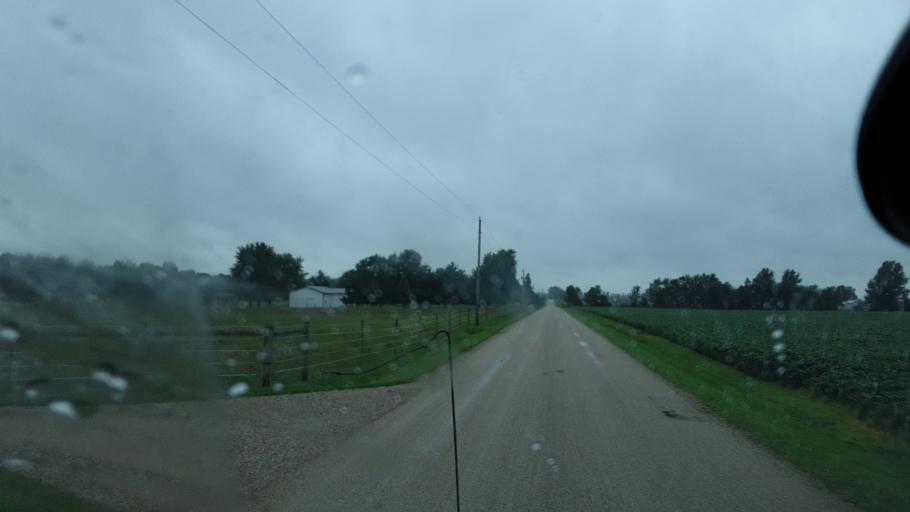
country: US
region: Indiana
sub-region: Adams County
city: Berne
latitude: 40.7030
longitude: -84.8465
